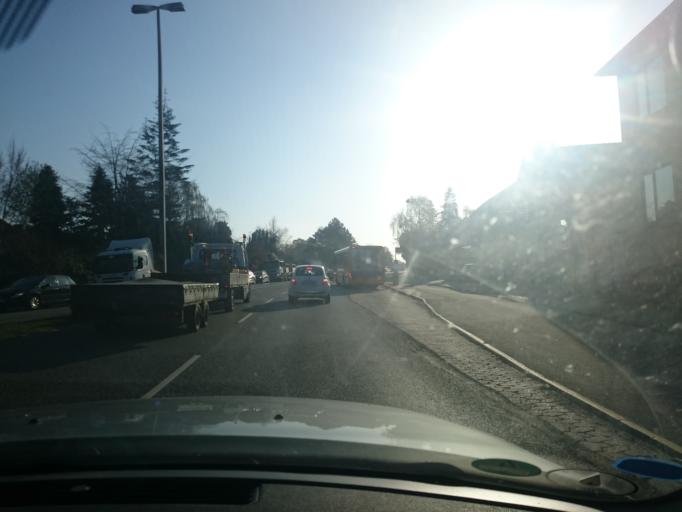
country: DK
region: Capital Region
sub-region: Gentofte Kommune
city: Charlottenlund
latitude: 55.7275
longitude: 12.5520
